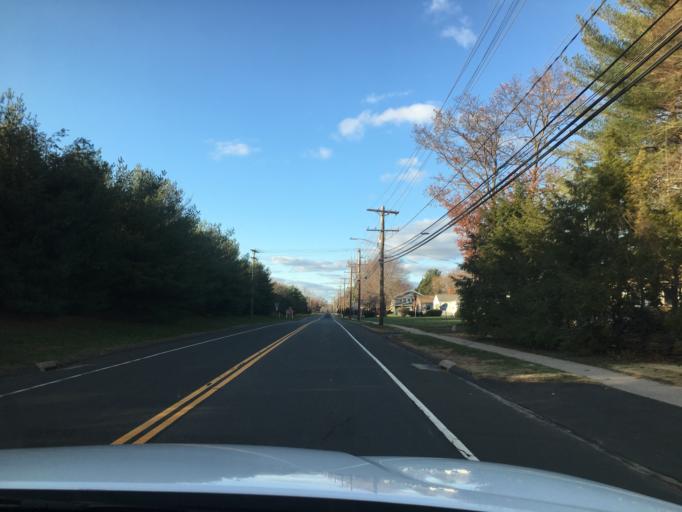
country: US
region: Connecticut
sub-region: Hartford County
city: Windsor Locks
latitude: 41.9134
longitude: -72.6591
